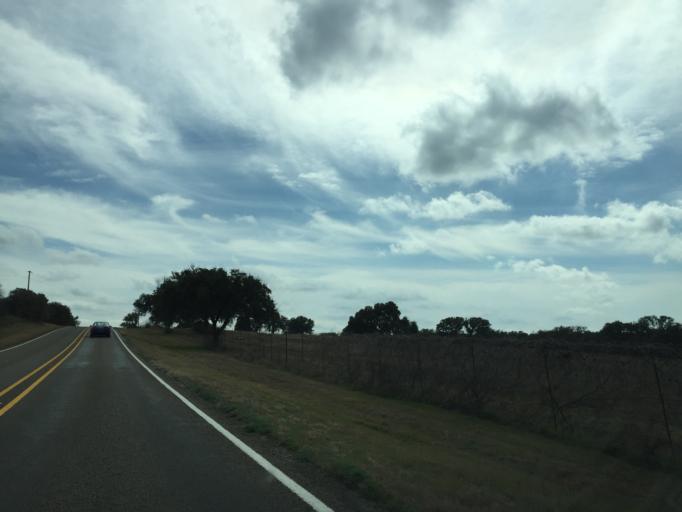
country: US
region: Texas
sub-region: Burnet County
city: Granite Shoals
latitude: 30.5161
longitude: -98.4436
